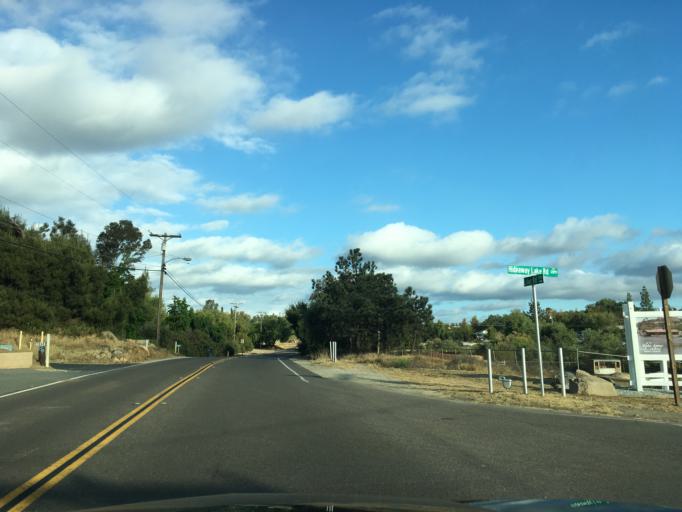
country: US
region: California
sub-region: San Diego County
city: Valley Center
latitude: 33.2361
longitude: -117.0513
